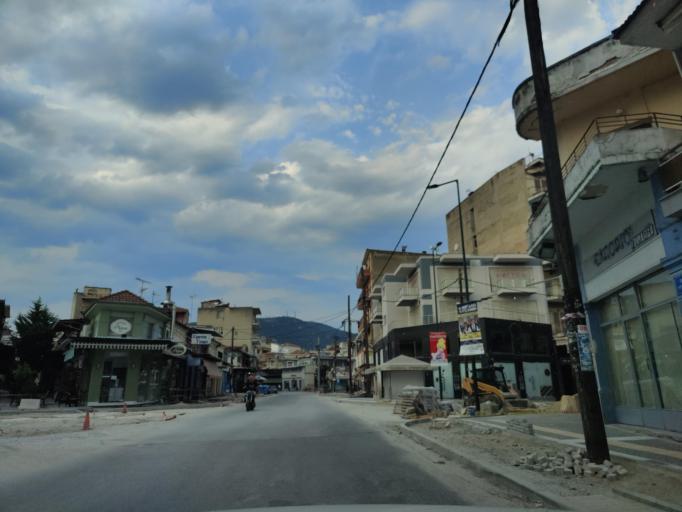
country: GR
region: East Macedonia and Thrace
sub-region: Nomos Dramas
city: Drama
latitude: 41.1492
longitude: 24.1449
